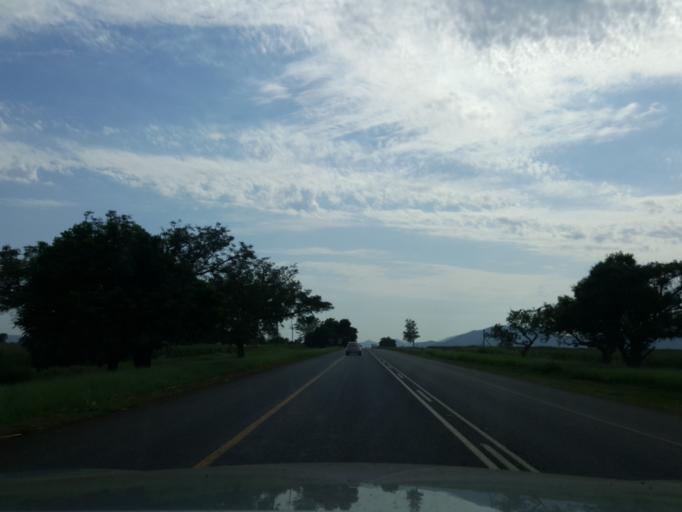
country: SZ
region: Hhohho
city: Ntfonjeni
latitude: -25.5069
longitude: 31.4877
